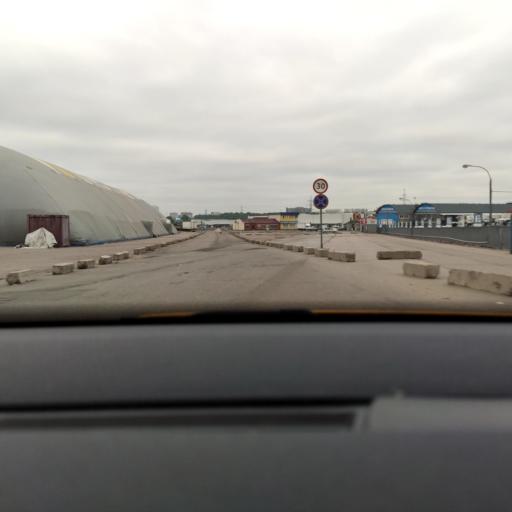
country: RU
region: Moscow
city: Vatutino
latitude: 55.8984
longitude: 37.6761
